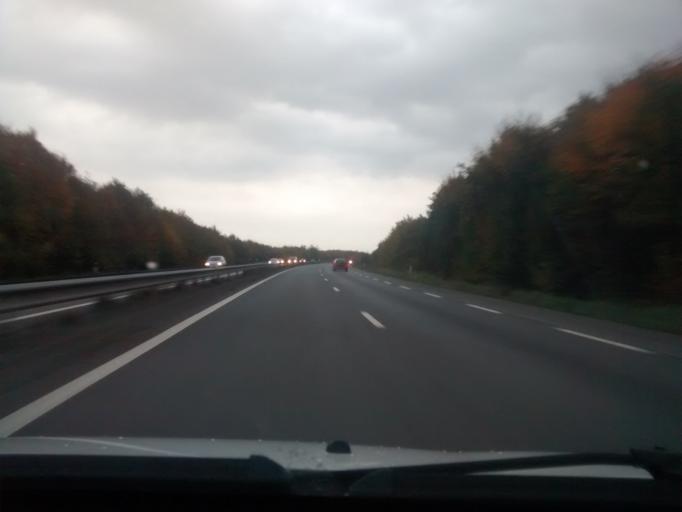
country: FR
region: Brittany
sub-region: Departement d'Ille-et-Vilaine
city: Saint-Domineuc
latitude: 48.3501
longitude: -1.8638
